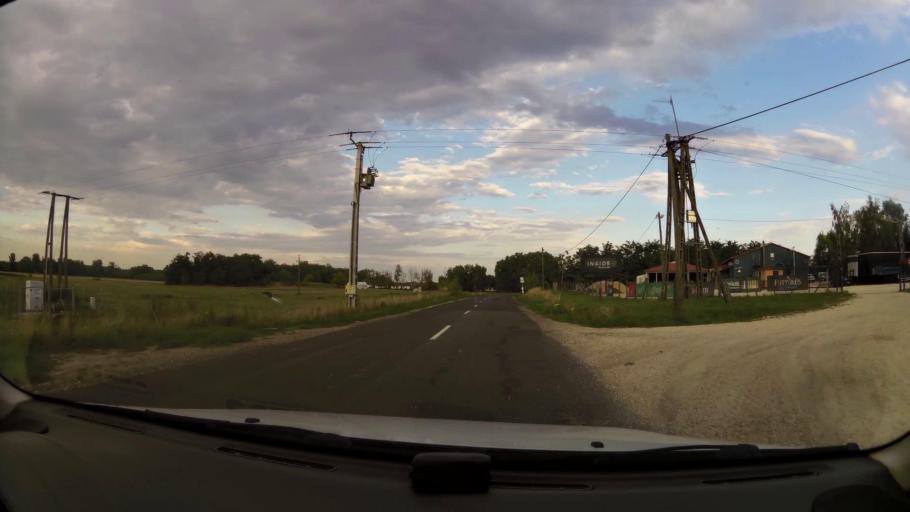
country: HU
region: Pest
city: Tapiobicske
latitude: 47.3541
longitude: 19.7006
